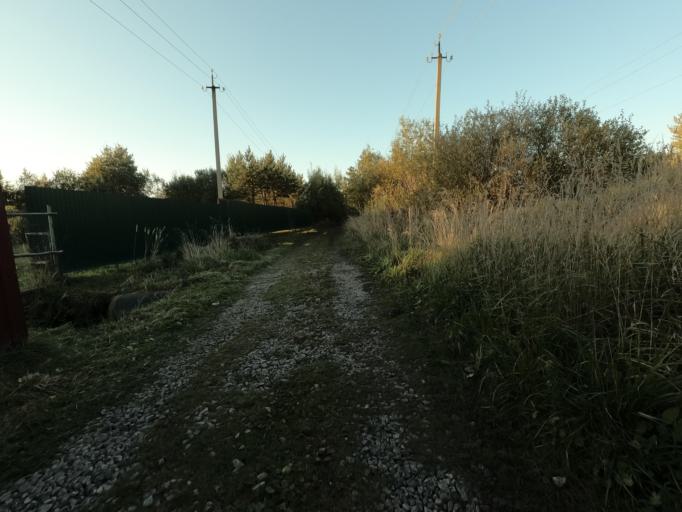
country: RU
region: Leningrad
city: Nikol'skoye
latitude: 59.7116
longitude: 30.7973
